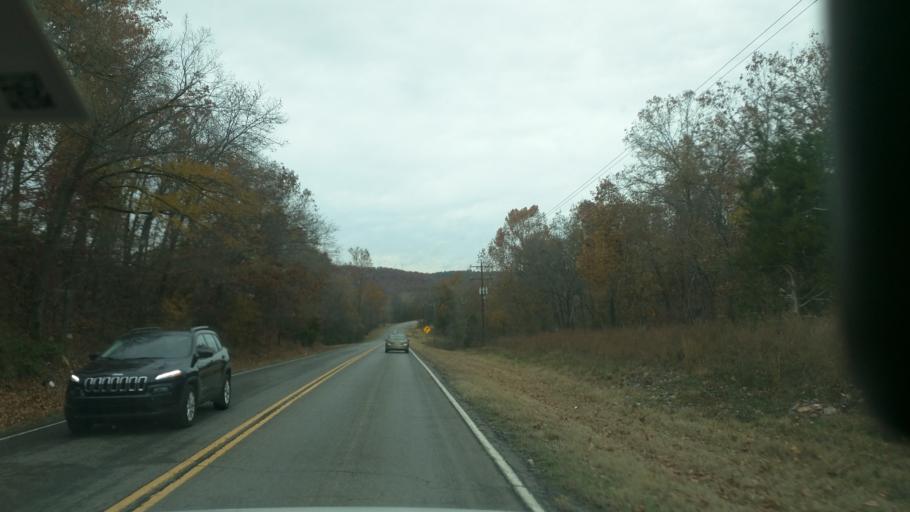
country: US
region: Oklahoma
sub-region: Cherokee County
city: Park Hill
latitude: 35.9089
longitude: -94.8312
